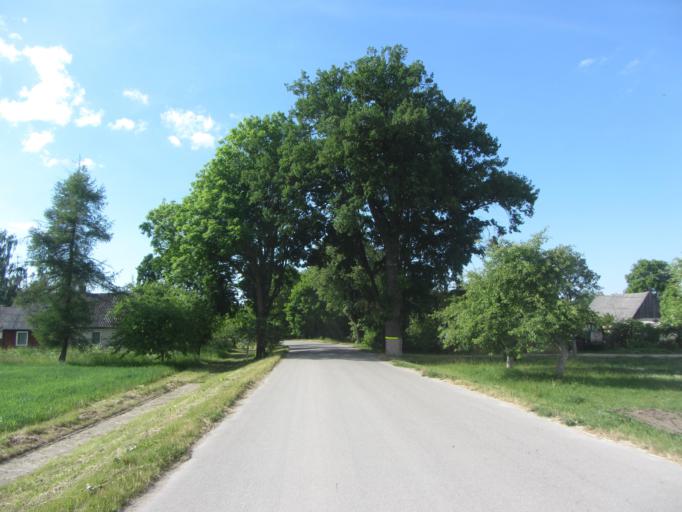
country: LT
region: Panevezys
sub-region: Birzai
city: Birzai
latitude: 56.2401
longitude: 24.6903
